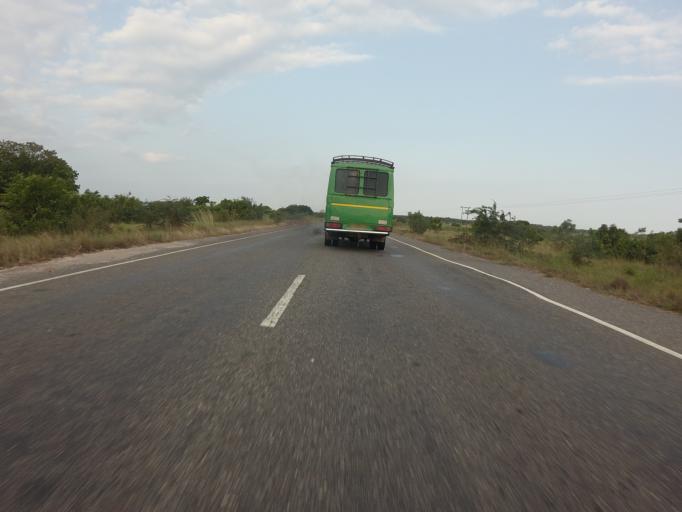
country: GH
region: Volta
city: Anloga
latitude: 6.0897
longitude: 0.5328
